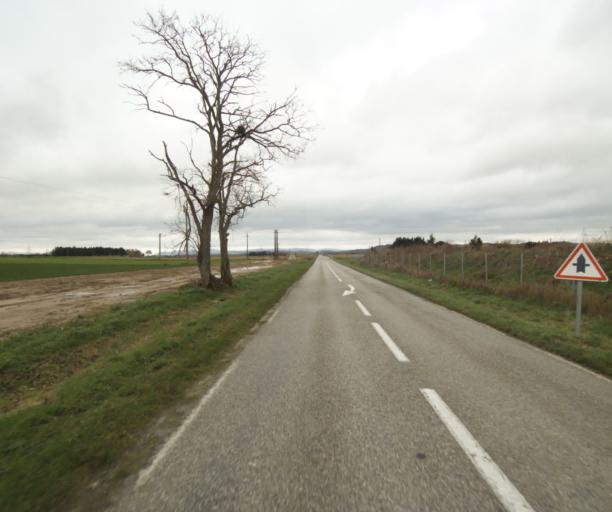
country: FR
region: Midi-Pyrenees
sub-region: Departement de l'Ariege
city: Mazeres
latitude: 43.2124
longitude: 1.6304
